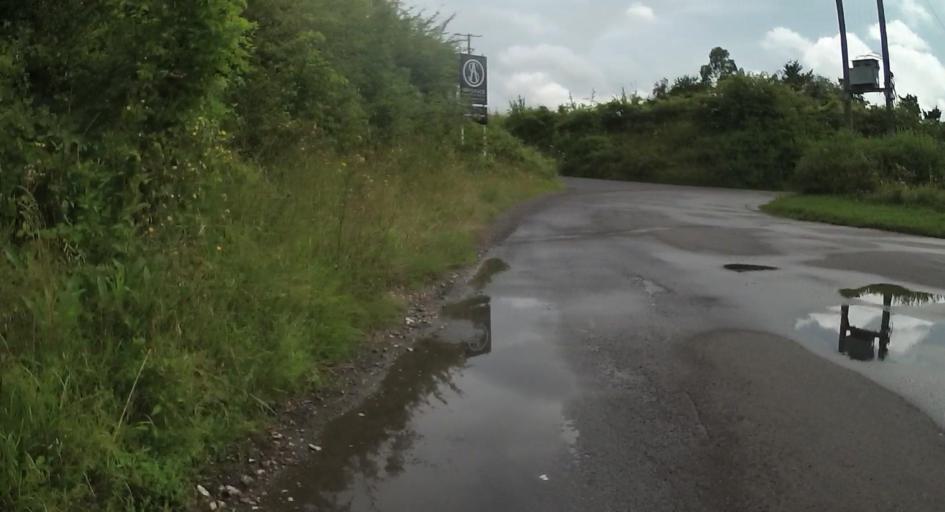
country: GB
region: England
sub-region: Hampshire
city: Andover
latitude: 51.2245
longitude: -1.4290
